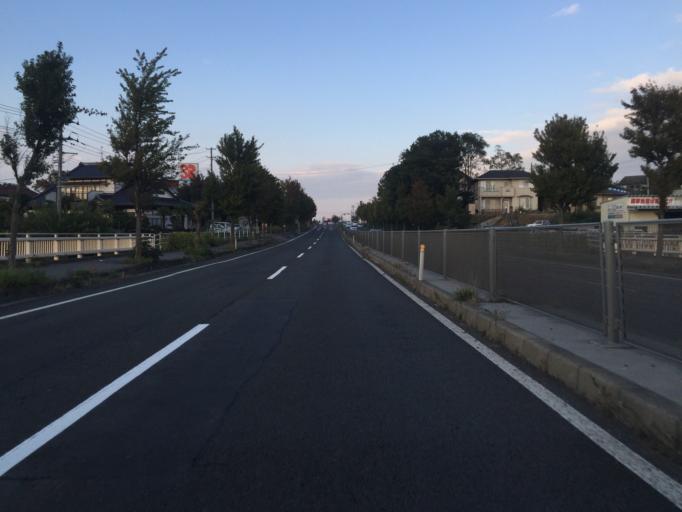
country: JP
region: Fukushima
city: Motomiya
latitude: 37.4995
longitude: 140.3900
